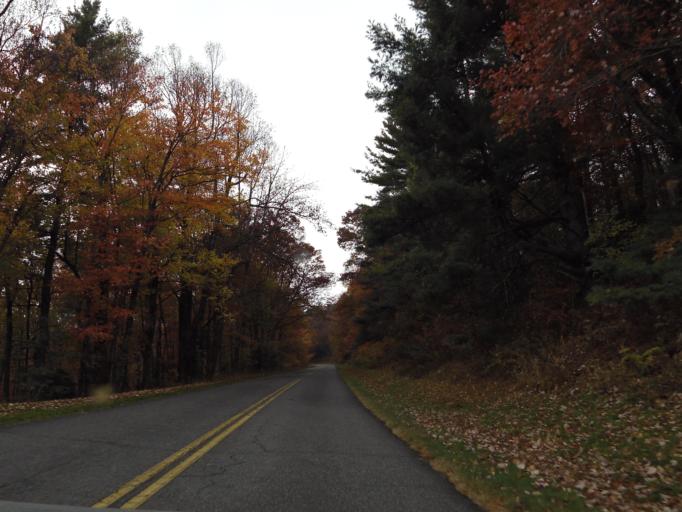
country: US
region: North Carolina
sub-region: Ashe County
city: West Jefferson
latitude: 36.2773
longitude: -81.4203
